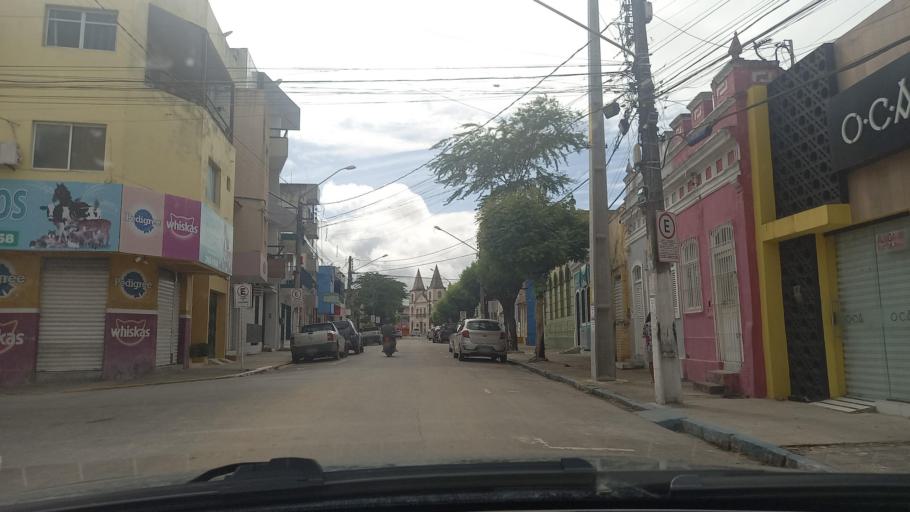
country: BR
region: Pernambuco
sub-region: Vitoria De Santo Antao
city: Vitoria de Santo Antao
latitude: -8.1174
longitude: -35.2945
